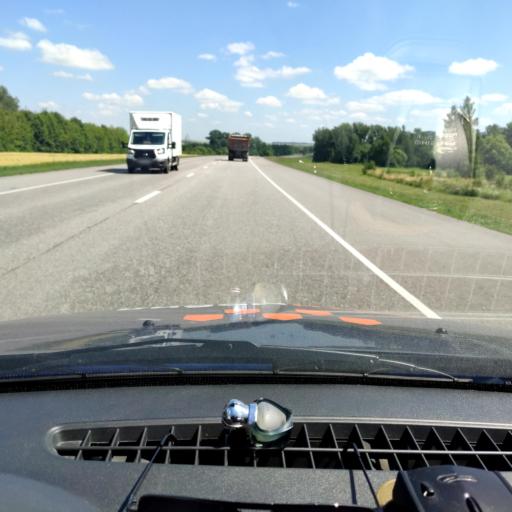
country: RU
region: Orjol
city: Orel
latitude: 52.8498
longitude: 36.2449
